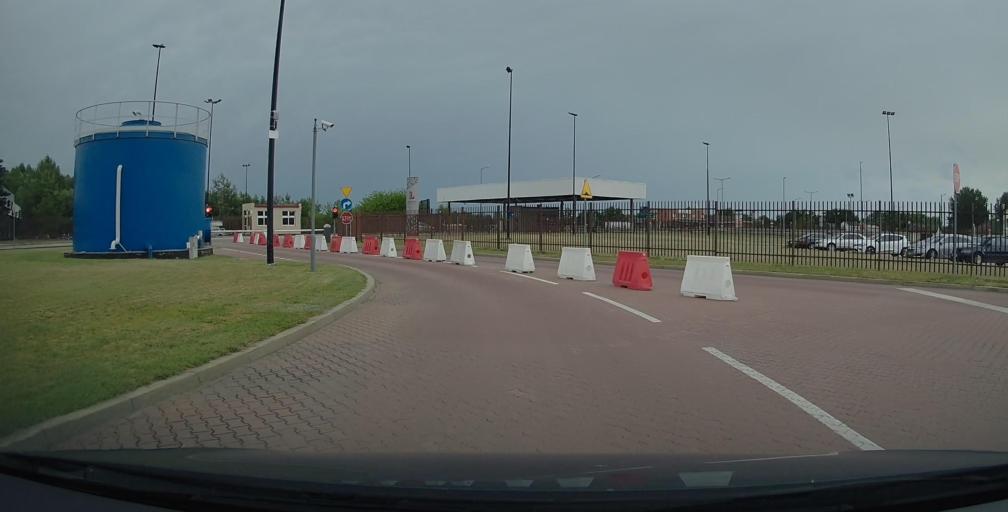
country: PL
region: Lublin Voivodeship
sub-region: Powiat bialski
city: Terespol
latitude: 52.0706
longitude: 23.6421
